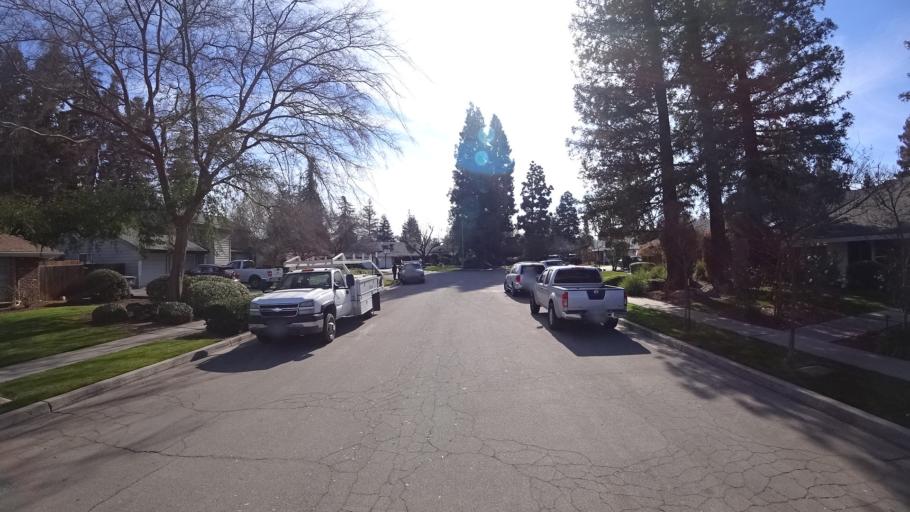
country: US
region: California
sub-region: Fresno County
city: Clovis
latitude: 36.8642
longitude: -119.7744
